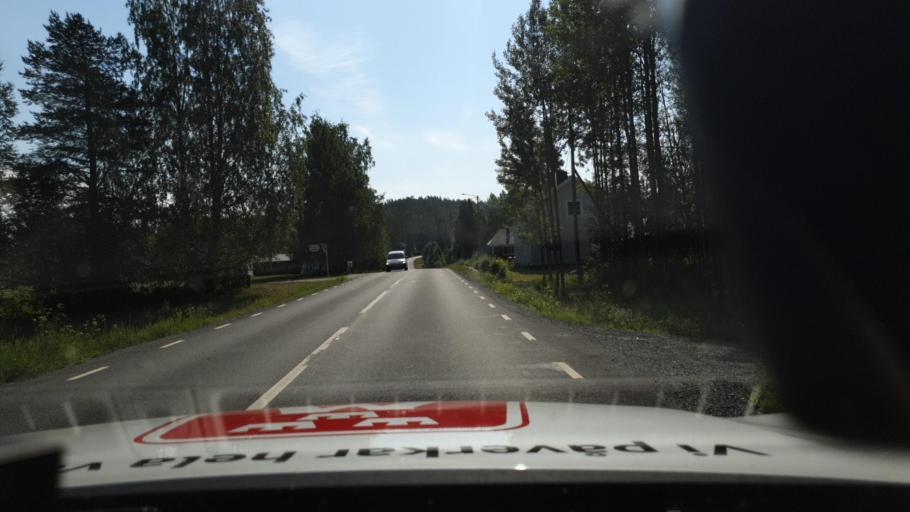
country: SE
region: Norrbotten
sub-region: Bodens Kommun
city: Saevast
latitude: 65.8321
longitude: 21.8731
